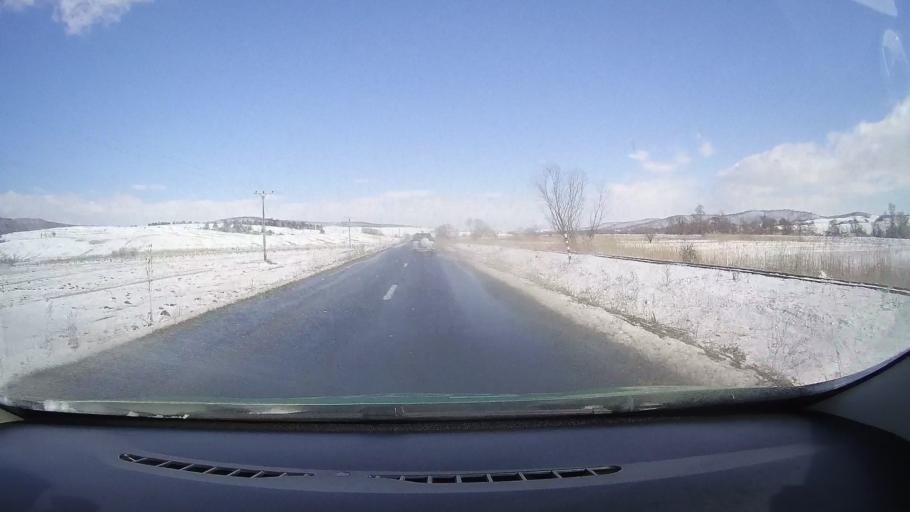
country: RO
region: Sibiu
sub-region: Comuna Rosia
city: Rosia
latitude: 45.8063
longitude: 24.3558
